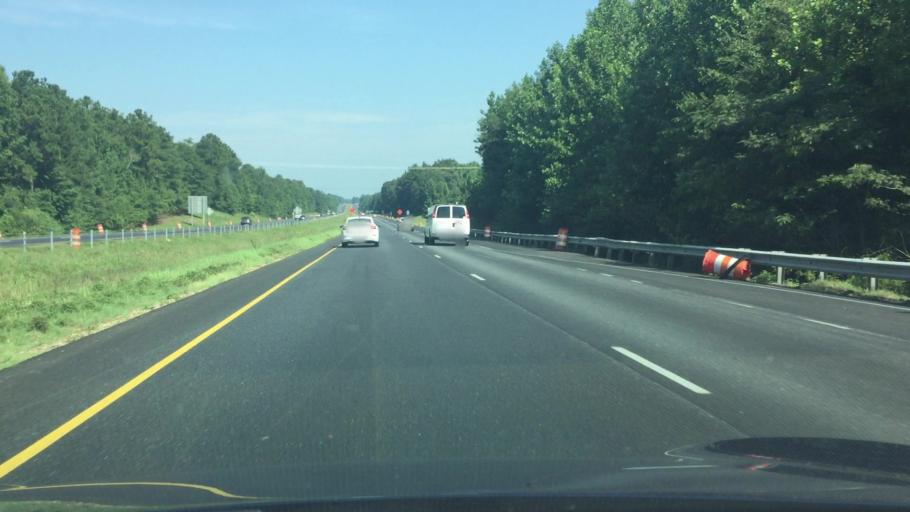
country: US
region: Alabama
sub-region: Autauga County
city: Marbury
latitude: 32.7429
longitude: -86.5467
